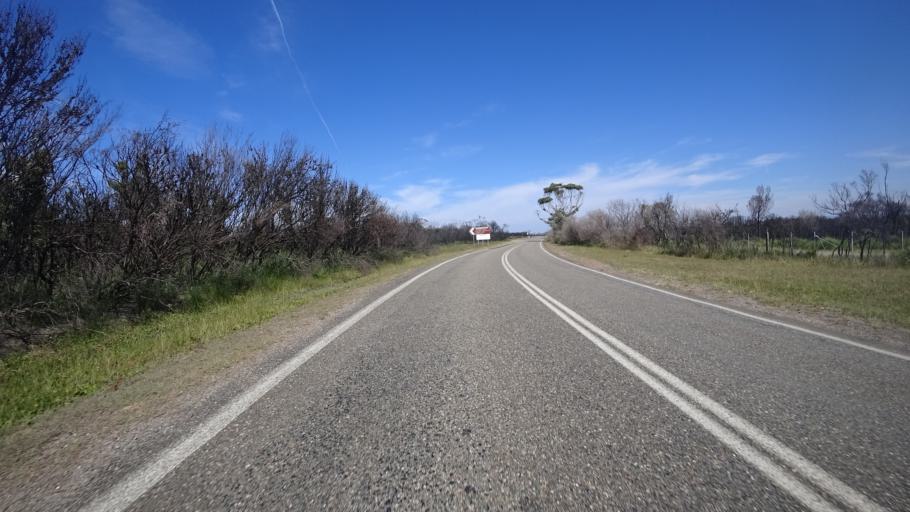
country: AU
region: New South Wales
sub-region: Shoalhaven Shire
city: Falls Creek
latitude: -35.1525
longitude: 150.7075
